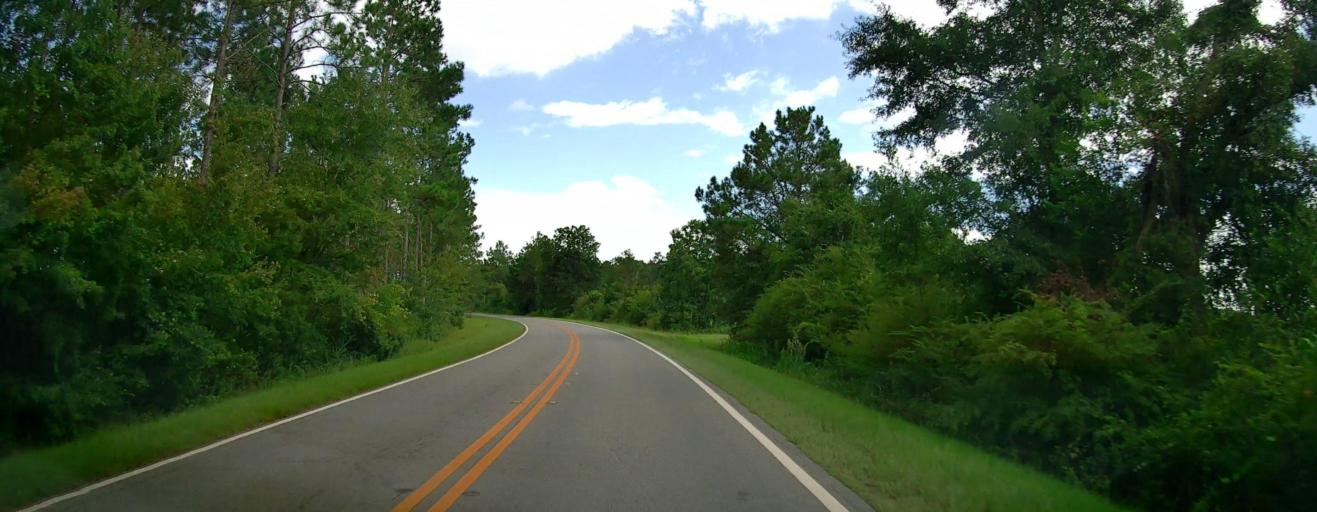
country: US
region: Georgia
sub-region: Ben Hill County
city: Fitzgerald
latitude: 31.6723
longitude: -83.1914
